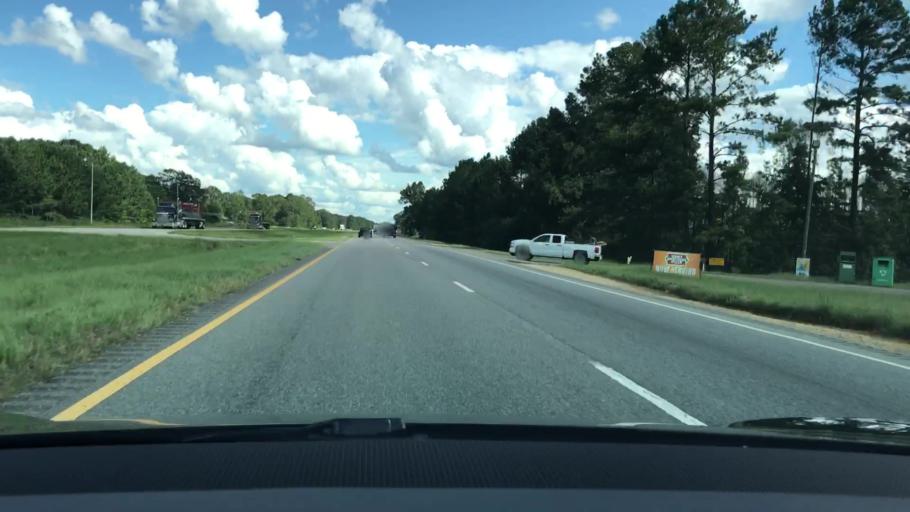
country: US
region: Alabama
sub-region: Montgomery County
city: Taylor
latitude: 32.0519
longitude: -86.0438
